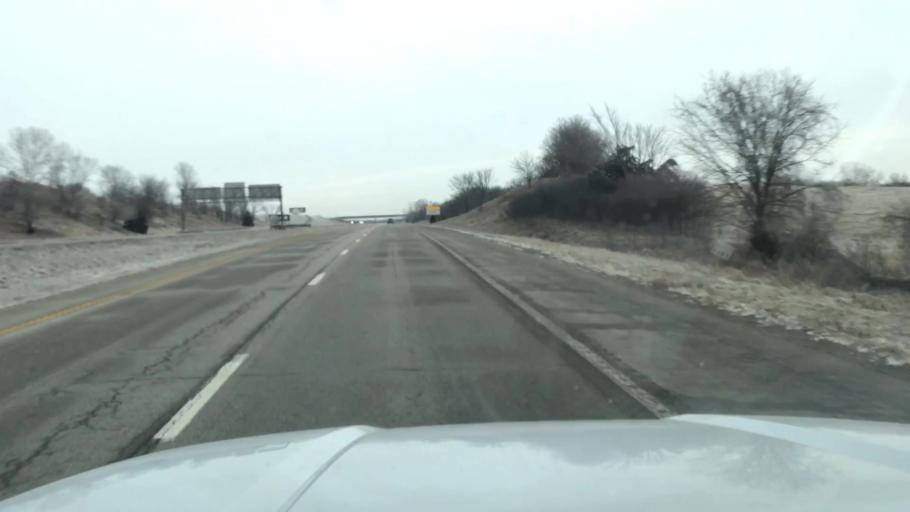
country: US
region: Missouri
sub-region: Andrew County
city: Savannah
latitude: 39.8909
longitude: -94.8571
